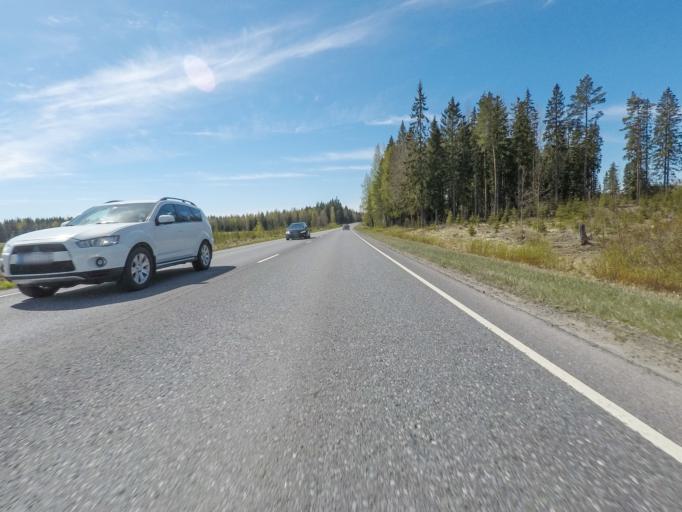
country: FI
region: Haeme
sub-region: Forssa
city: Humppila
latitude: 60.9658
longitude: 23.3919
